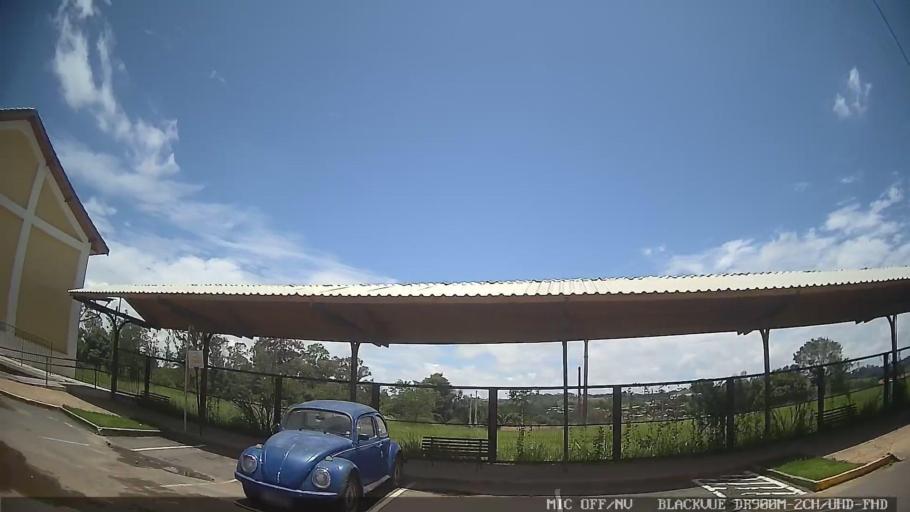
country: BR
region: Sao Paulo
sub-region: Laranjal Paulista
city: Laranjal Paulista
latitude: -23.0471
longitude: -47.8390
